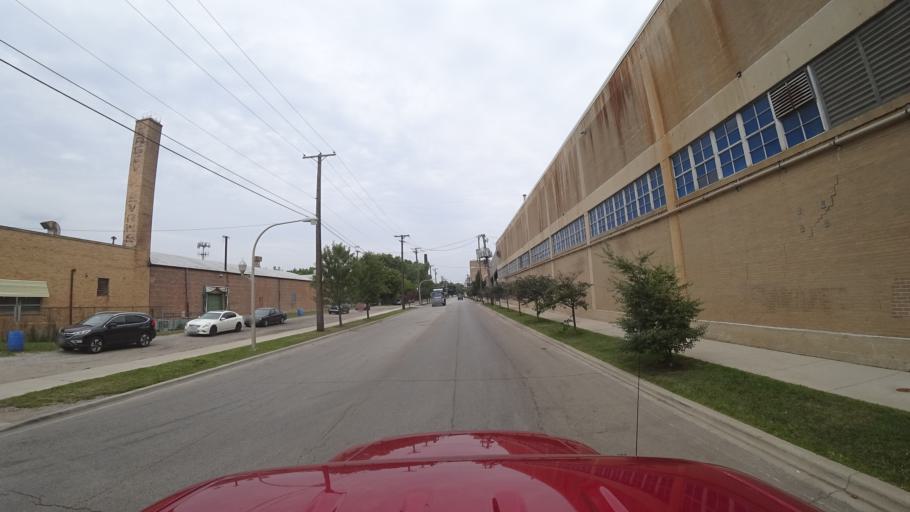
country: US
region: Illinois
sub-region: Cook County
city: Chicago
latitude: 41.8279
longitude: -87.6557
